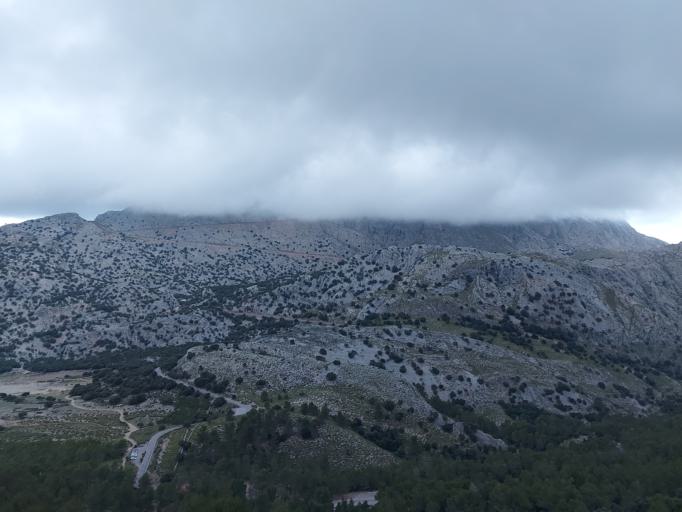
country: ES
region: Balearic Islands
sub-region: Illes Balears
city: Fornalutx
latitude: 39.7846
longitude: 2.8010
